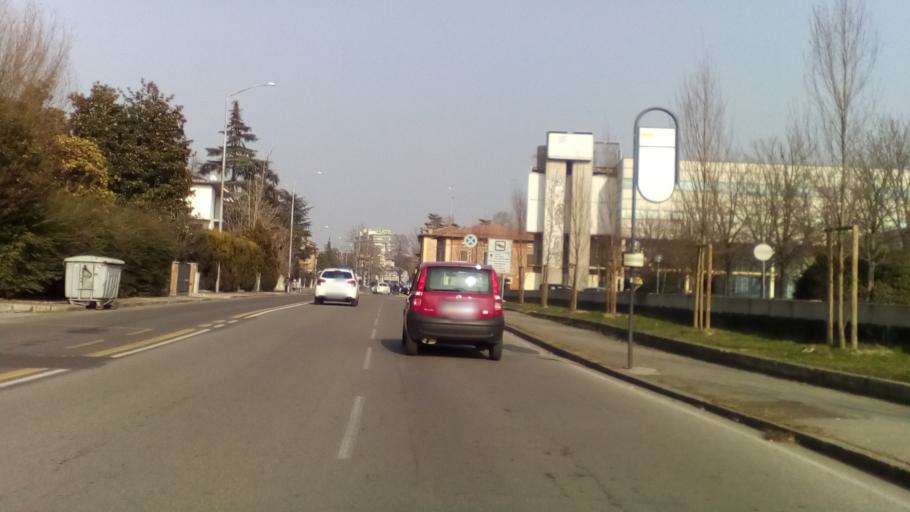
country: IT
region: Emilia-Romagna
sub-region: Provincia di Modena
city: Modena
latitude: 44.6357
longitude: 10.9385
